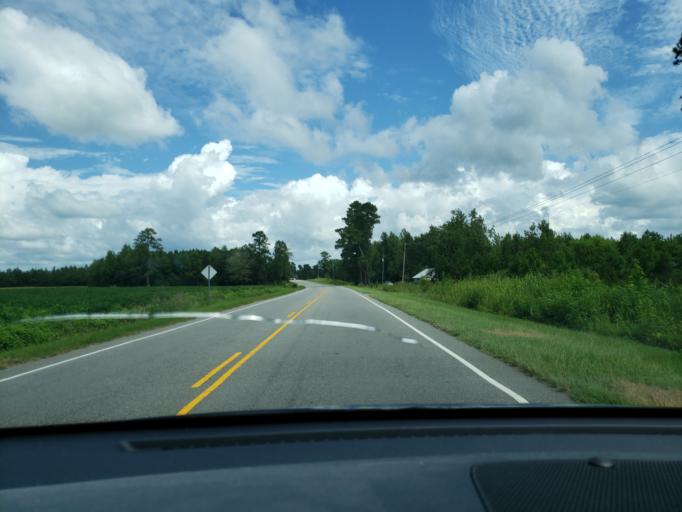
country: US
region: North Carolina
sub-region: Columbus County
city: Brunswick
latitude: 34.2086
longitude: -78.7601
